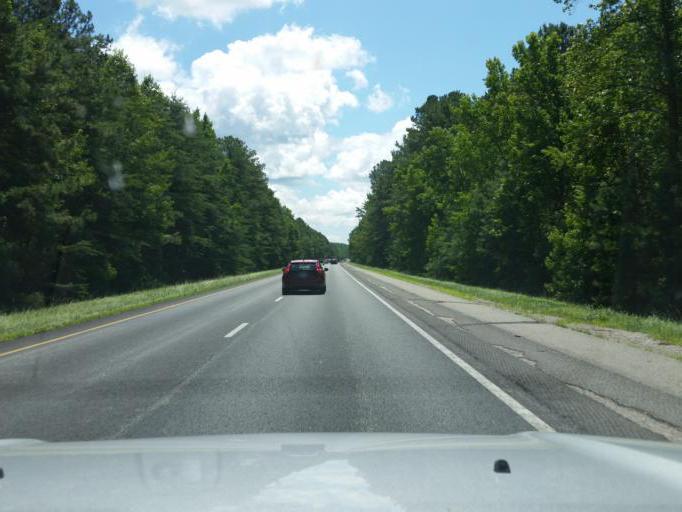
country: US
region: Virginia
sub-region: King William County
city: West Point
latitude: 37.4592
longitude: -76.8819
